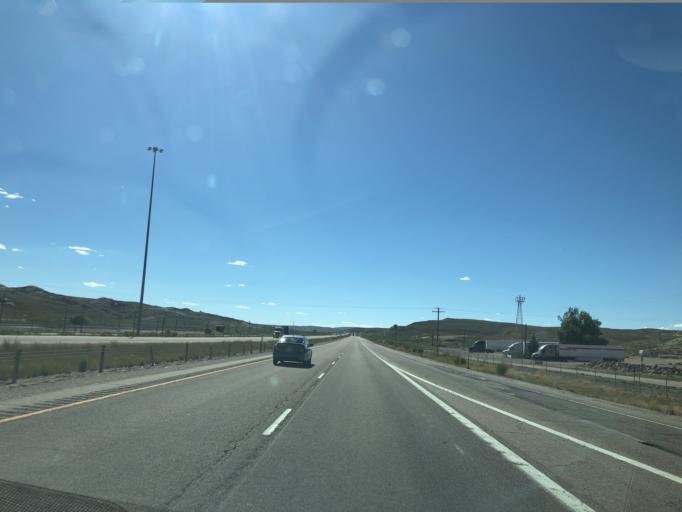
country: US
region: Wyoming
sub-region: Sweetwater County
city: Rock Springs
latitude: 41.6791
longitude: -108.7850
